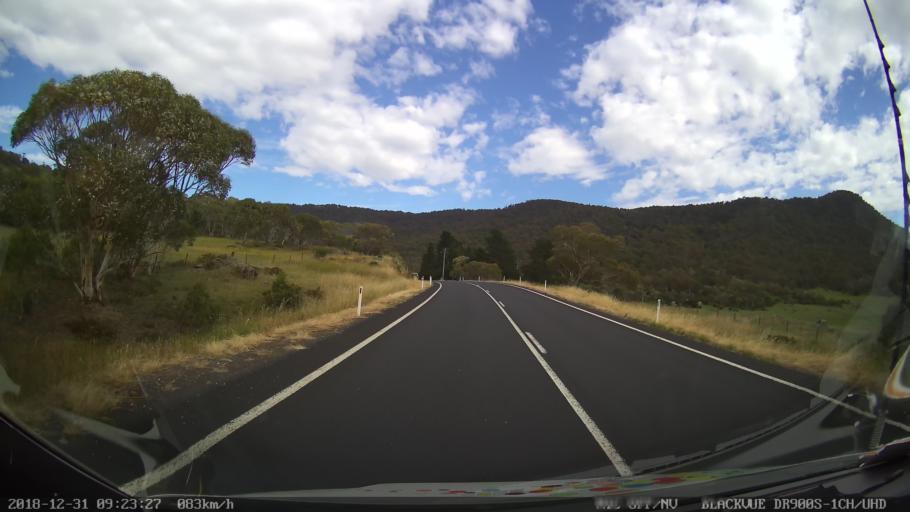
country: AU
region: New South Wales
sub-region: Snowy River
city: Jindabyne
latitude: -36.4376
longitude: 148.5340
